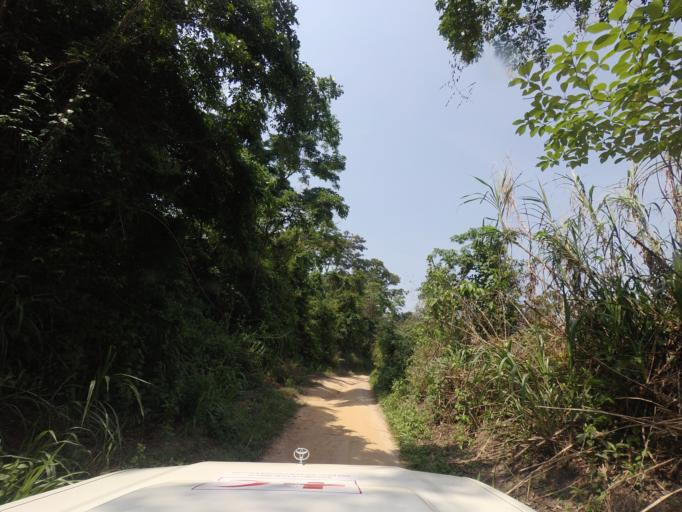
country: LR
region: Lofa
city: Voinjama
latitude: 8.5055
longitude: -9.6368
